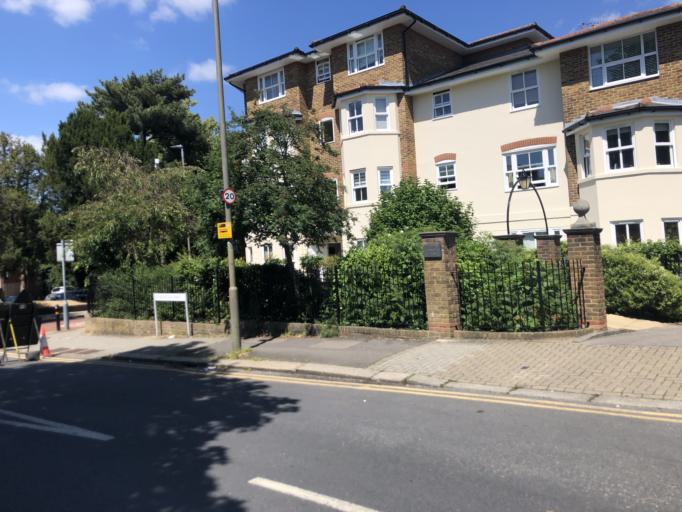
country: GB
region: England
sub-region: Greater London
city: Wandsworth
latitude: 51.4476
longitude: -0.2388
